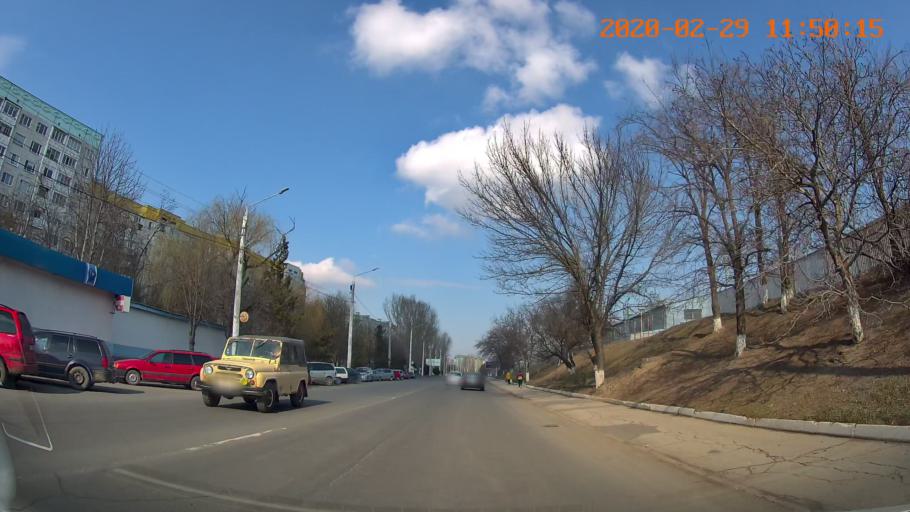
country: MD
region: Telenesti
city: Ribnita
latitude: 47.7567
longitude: 28.9912
